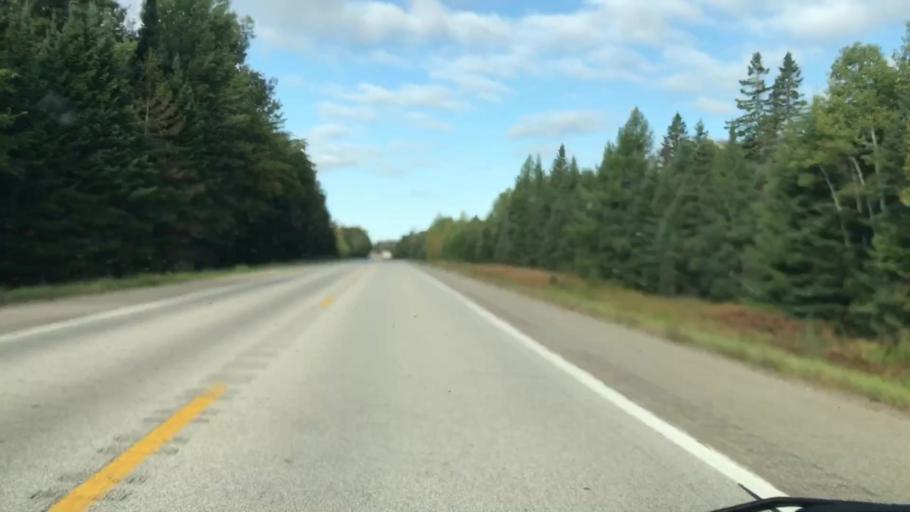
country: US
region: Michigan
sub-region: Luce County
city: Newberry
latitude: 46.3320
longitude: -85.0857
